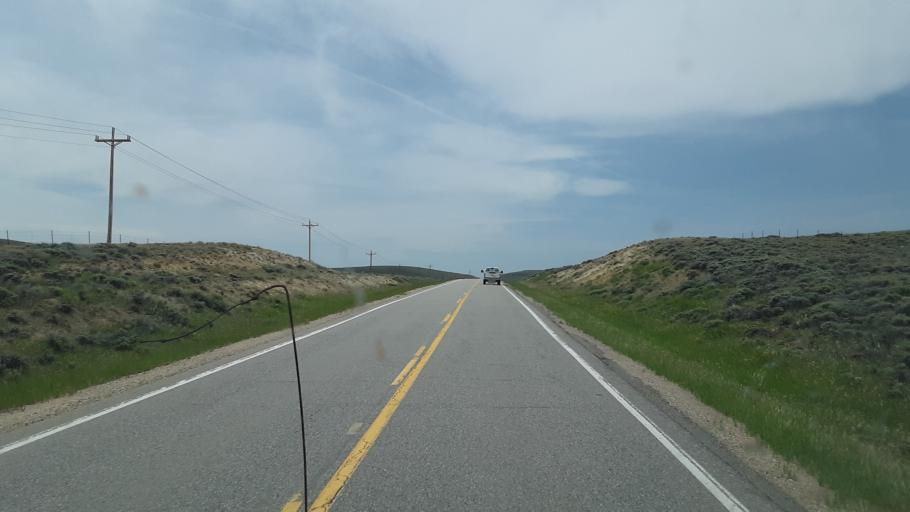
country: US
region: Colorado
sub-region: Jackson County
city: Walden
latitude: 40.6723
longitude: -106.3809
